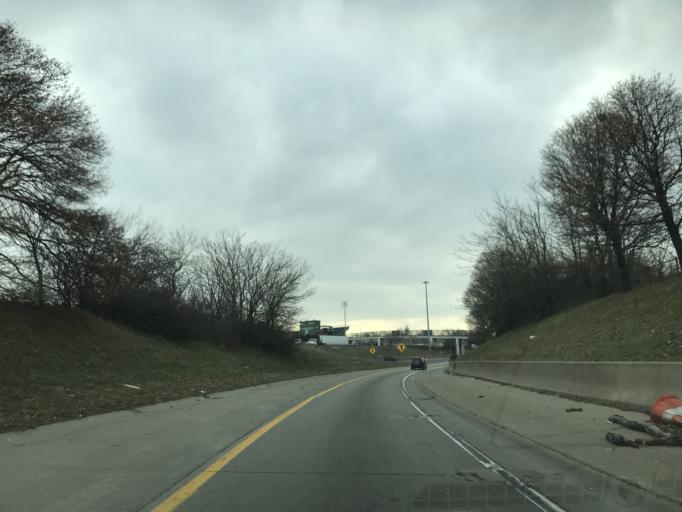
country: US
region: Michigan
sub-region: Wayne County
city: Detroit
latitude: 42.3593
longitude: -83.0778
